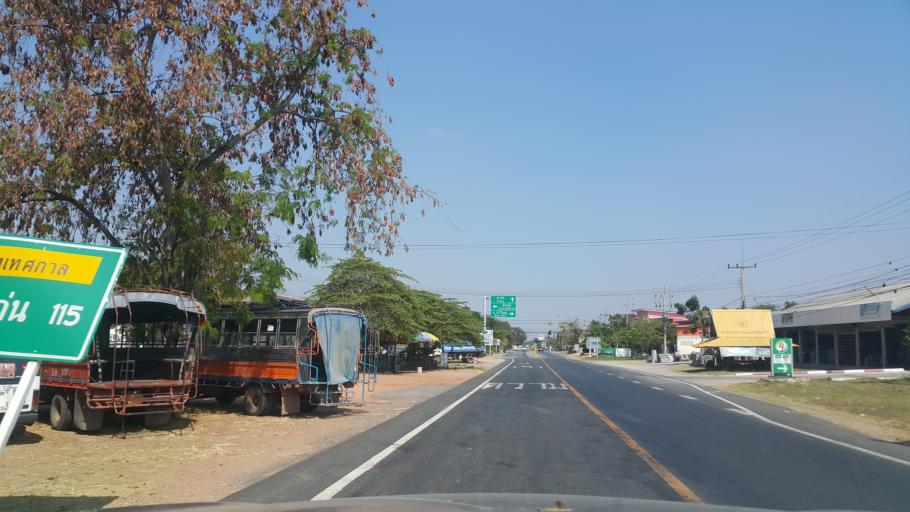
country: TH
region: Nakhon Ratchasima
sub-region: Amphoe Kaeng Sanam Nang
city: Kaeng Sanam Nang
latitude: 15.6882
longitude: 102.3309
